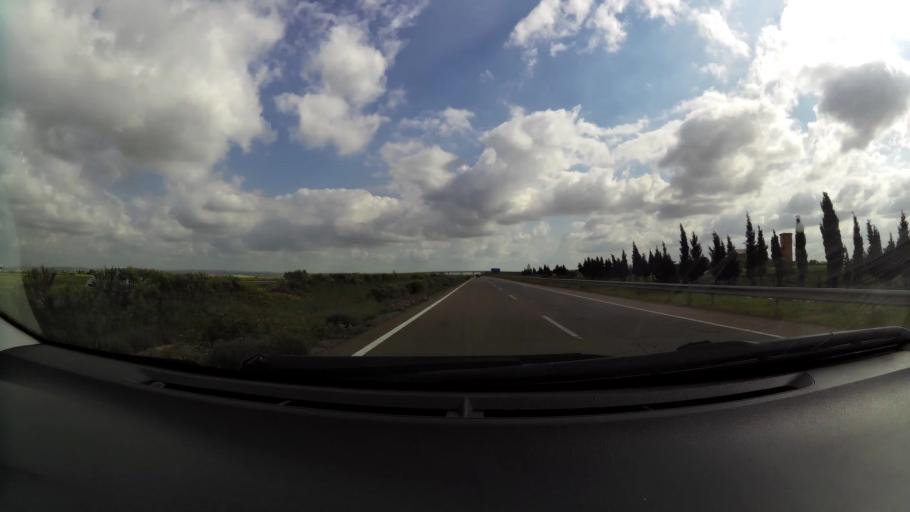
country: MA
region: Chaouia-Ouardigha
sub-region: Settat Province
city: Berrechid
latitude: 33.2020
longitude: -7.5758
